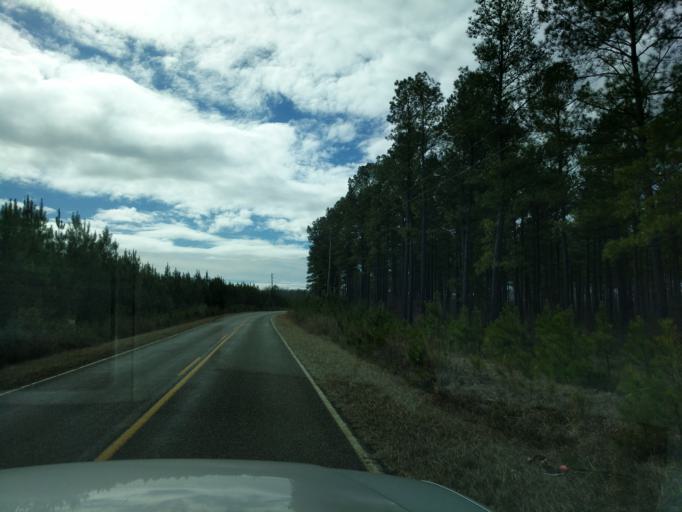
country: US
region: South Carolina
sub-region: Edgefield County
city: Edgefield
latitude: 33.8966
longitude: -82.0006
